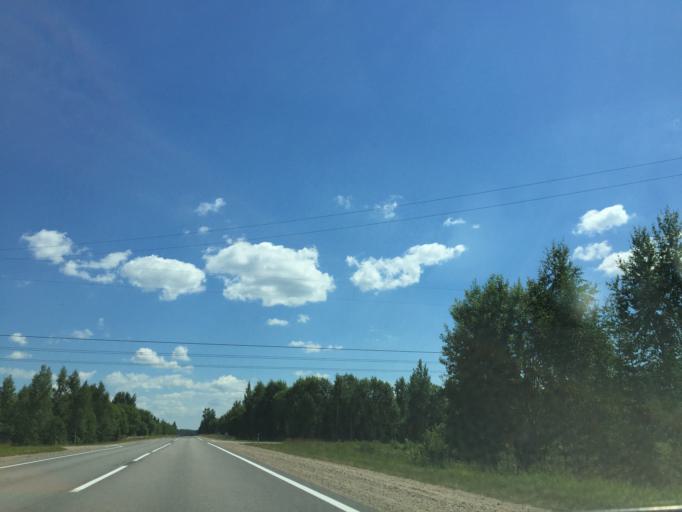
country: LV
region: Rezekne
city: Rezekne
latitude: 56.4857
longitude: 27.2814
